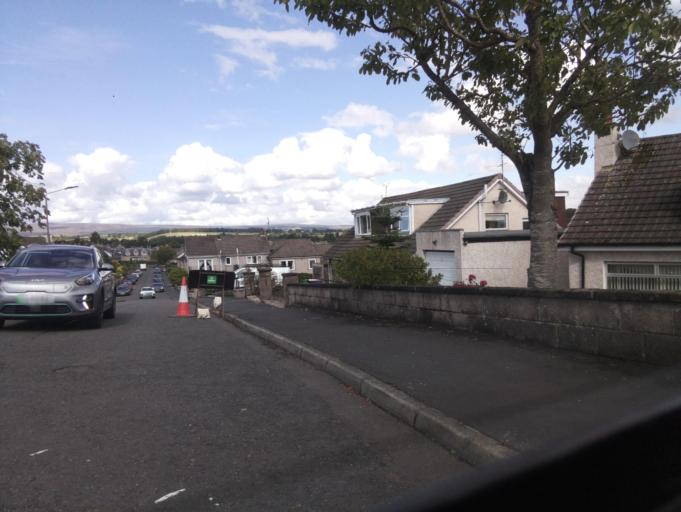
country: GB
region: Scotland
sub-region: Stirling
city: Dunblane
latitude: 56.1836
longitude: -3.9713
